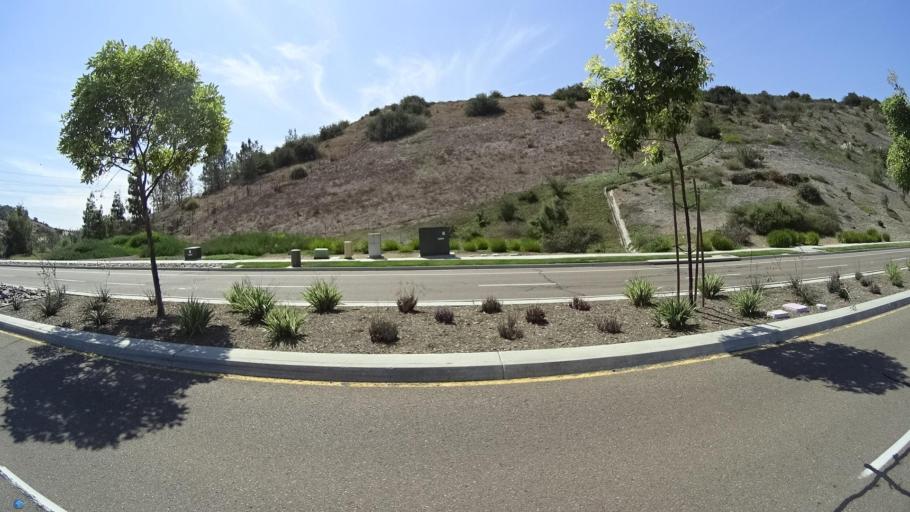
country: US
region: California
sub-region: San Diego County
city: La Presa
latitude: 32.6710
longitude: -116.9860
